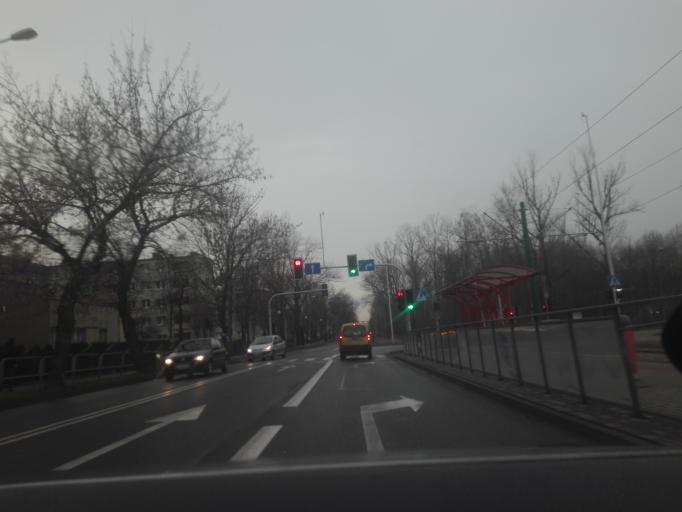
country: PL
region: Silesian Voivodeship
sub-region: Chorzow
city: Chorzow
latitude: 50.2700
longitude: 18.9752
